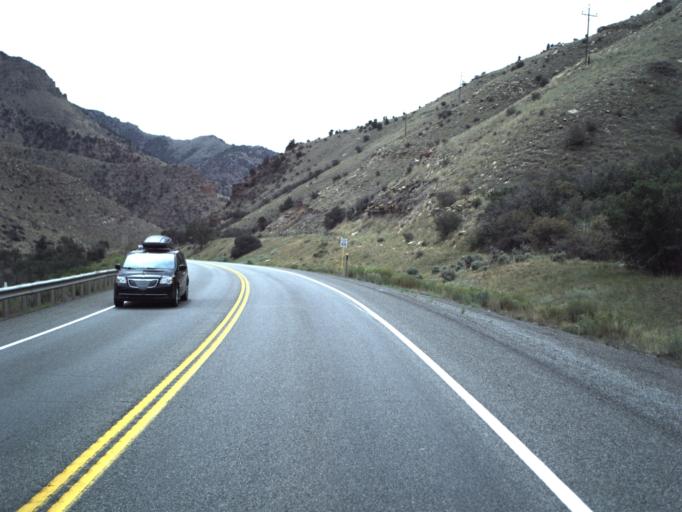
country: US
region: Utah
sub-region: Carbon County
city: Helper
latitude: 39.7434
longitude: -110.8801
